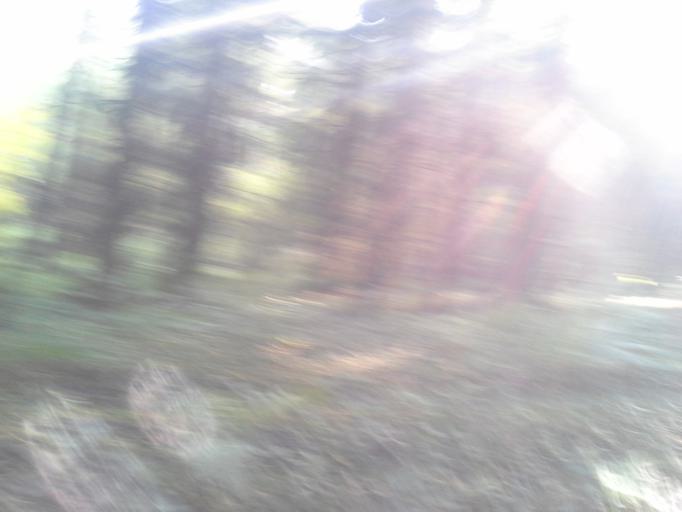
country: RU
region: Moskovskaya
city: Kievskij
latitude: 55.3859
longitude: 36.9232
